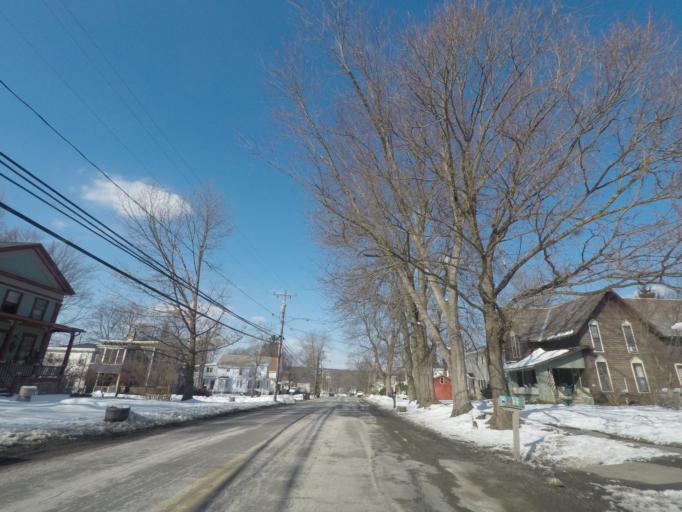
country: US
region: New York
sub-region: Saratoga County
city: Stillwater
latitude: 42.8993
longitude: -73.5631
